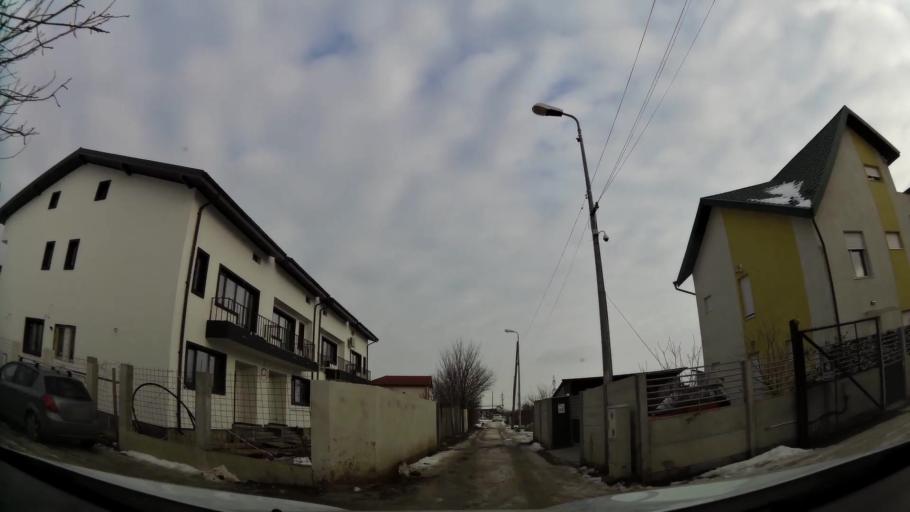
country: RO
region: Ilfov
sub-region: Comuna Popesti-Leordeni
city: Popesti-Leordeni
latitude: 44.4029
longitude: 26.1825
